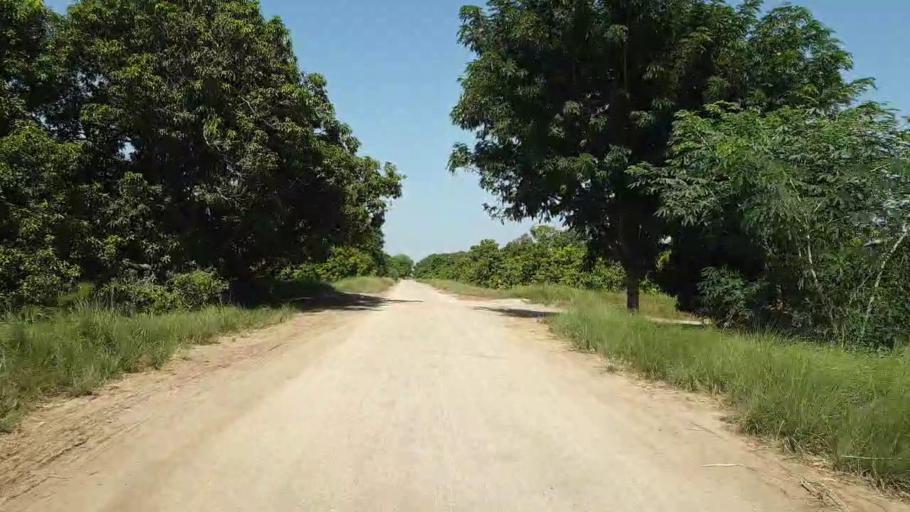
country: PK
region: Sindh
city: Tando Jam
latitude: 25.4335
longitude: 68.4599
